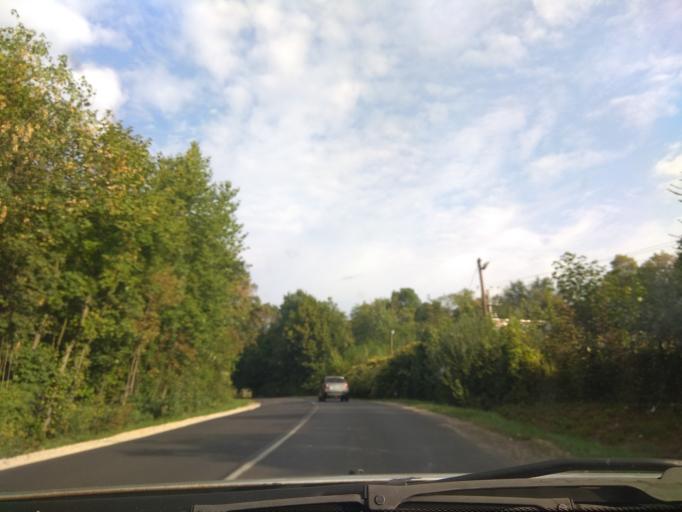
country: HU
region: Borsod-Abauj-Zemplen
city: Miskolc
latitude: 48.0817
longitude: 20.7712
